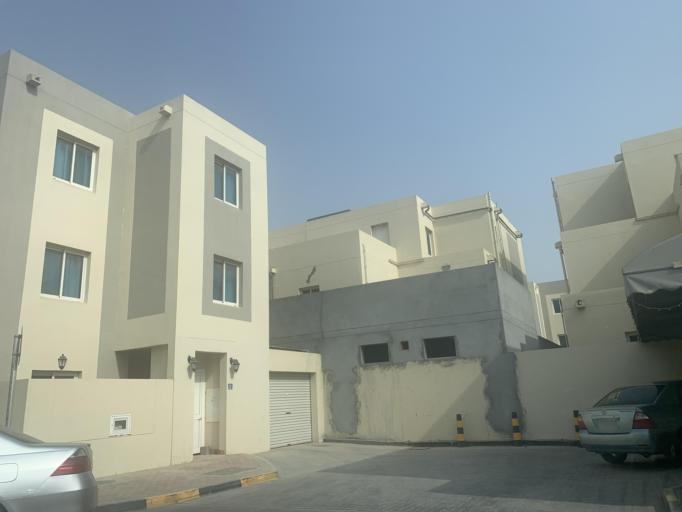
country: BH
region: Manama
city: Jidd Hafs
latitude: 26.2323
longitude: 50.4503
